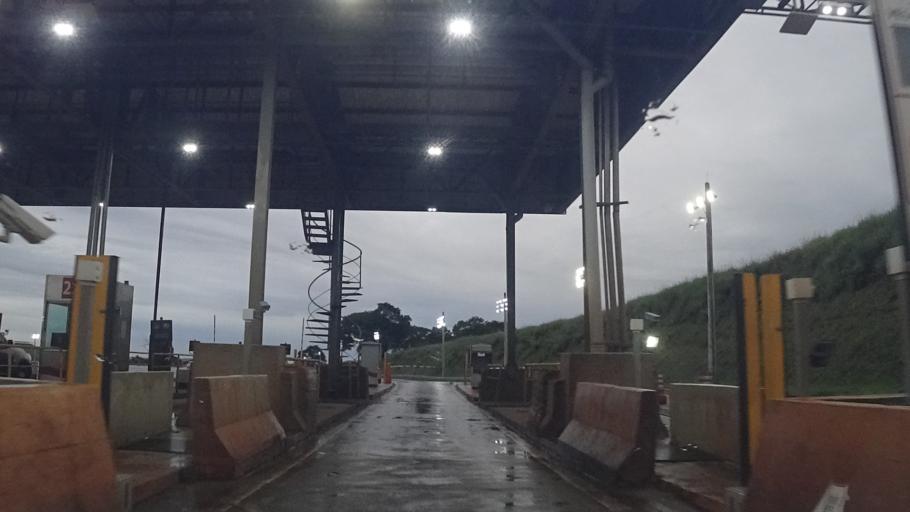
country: BR
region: Goias
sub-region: Goianapolis
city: Goianapolis
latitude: -16.4382
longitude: -49.0198
